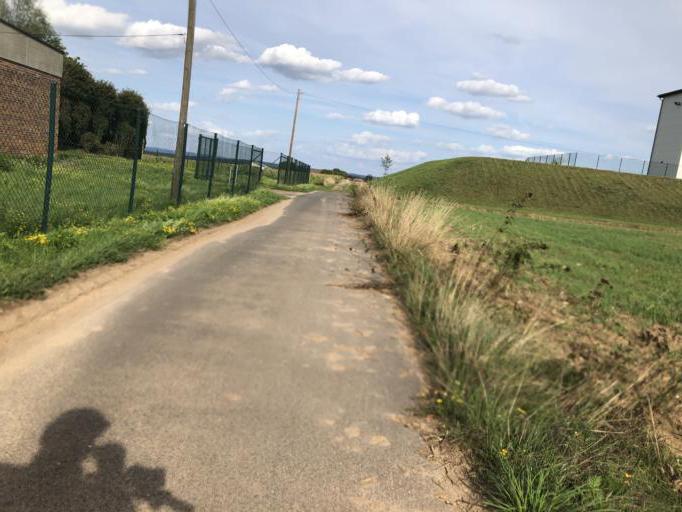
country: DE
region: Bavaria
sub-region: Regierungsbezirk Mittelfranken
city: Obermichelbach
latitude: 49.5423
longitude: 10.9424
